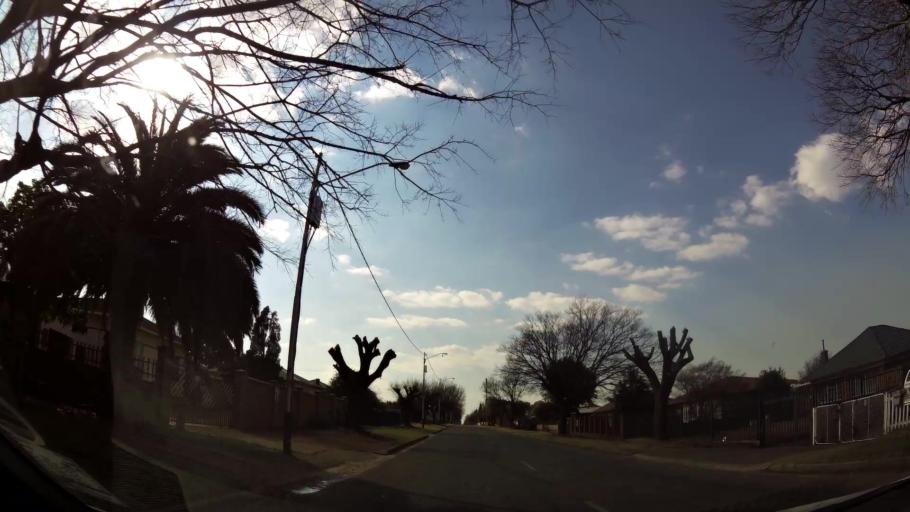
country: ZA
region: Gauteng
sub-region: Ekurhuleni Metropolitan Municipality
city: Germiston
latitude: -26.1739
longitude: 28.1727
